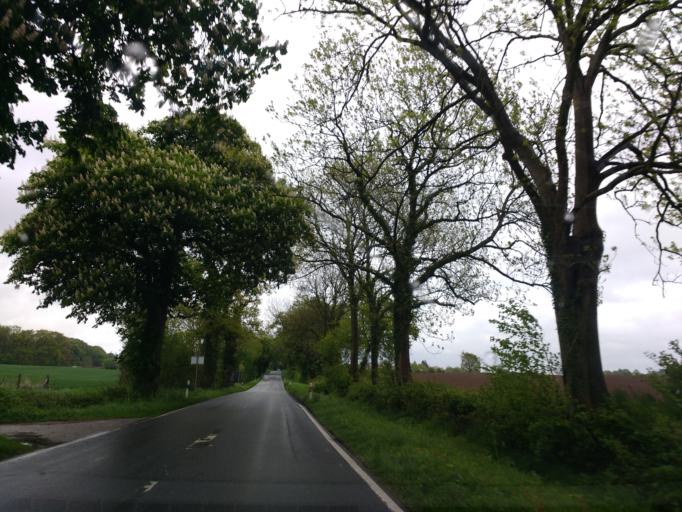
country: DE
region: Schleswig-Holstein
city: Loose
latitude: 54.5105
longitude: 9.9218
